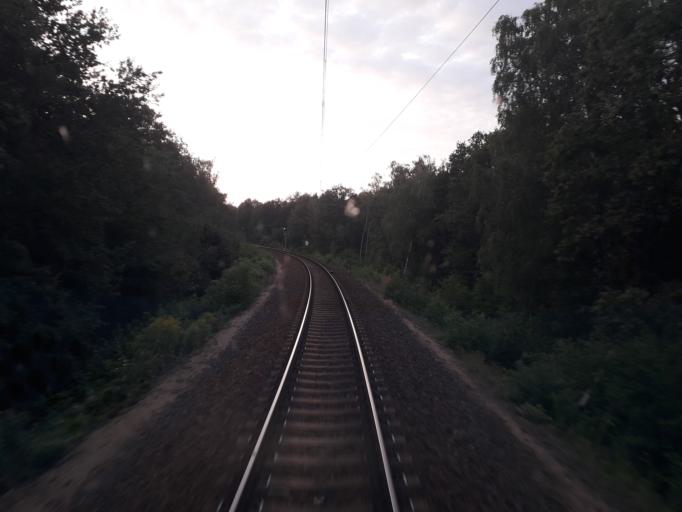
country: DE
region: Brandenburg
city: Hennigsdorf
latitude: 52.6571
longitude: 13.2014
